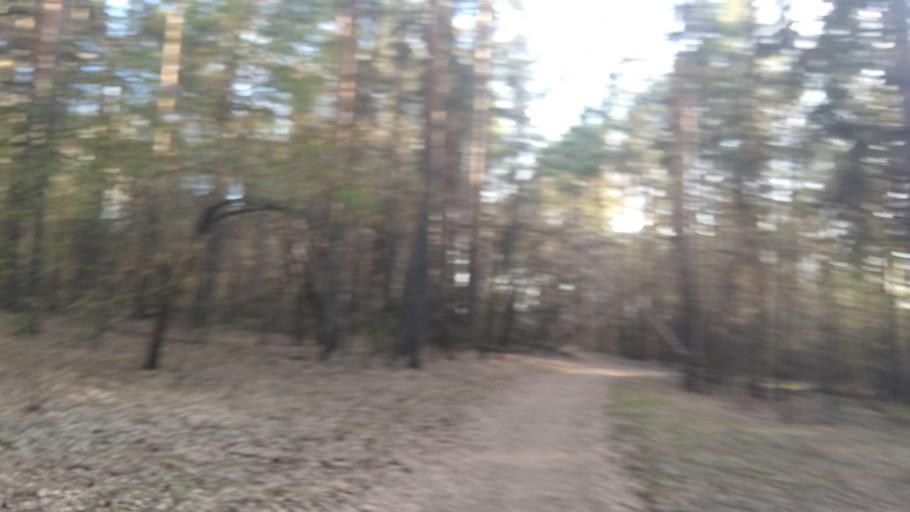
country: RU
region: Chelyabinsk
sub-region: Gorod Chelyabinsk
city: Chelyabinsk
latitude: 55.1494
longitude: 61.3327
